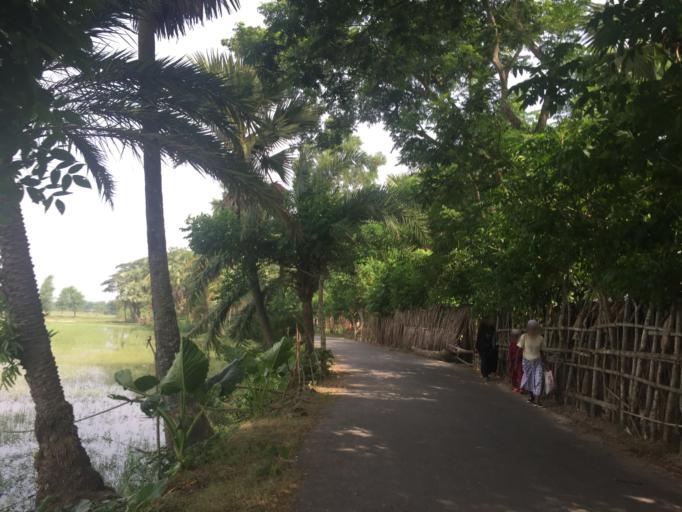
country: BD
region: Barisal
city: Mathba
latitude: 22.2118
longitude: 89.9238
